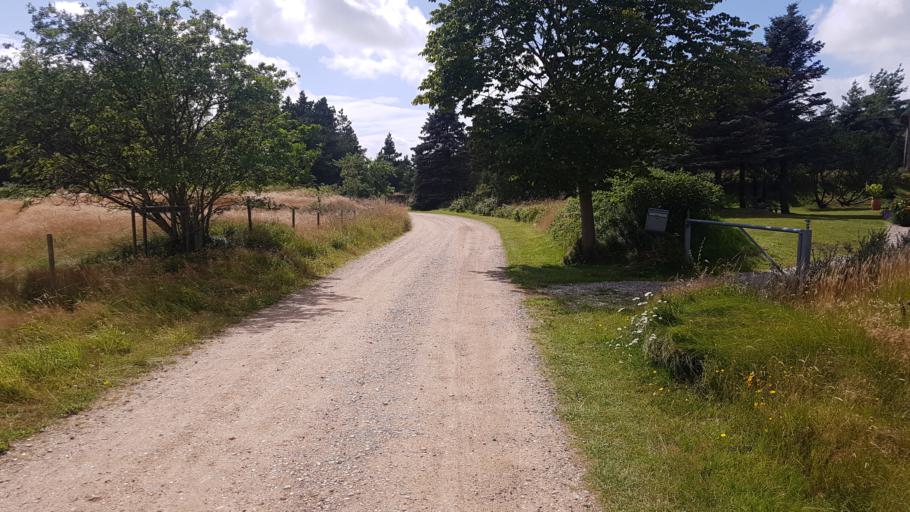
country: DE
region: Schleswig-Holstein
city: List
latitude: 55.1285
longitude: 8.5404
